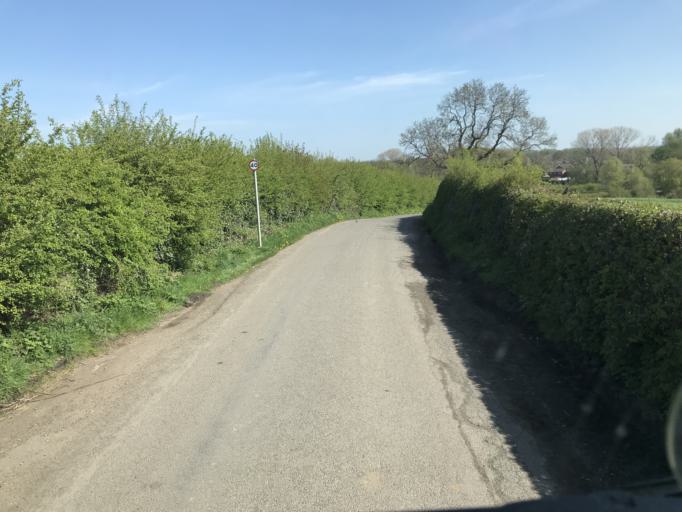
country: GB
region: England
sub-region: Cheshire East
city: Middlewich
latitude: 53.1953
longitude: -2.4625
